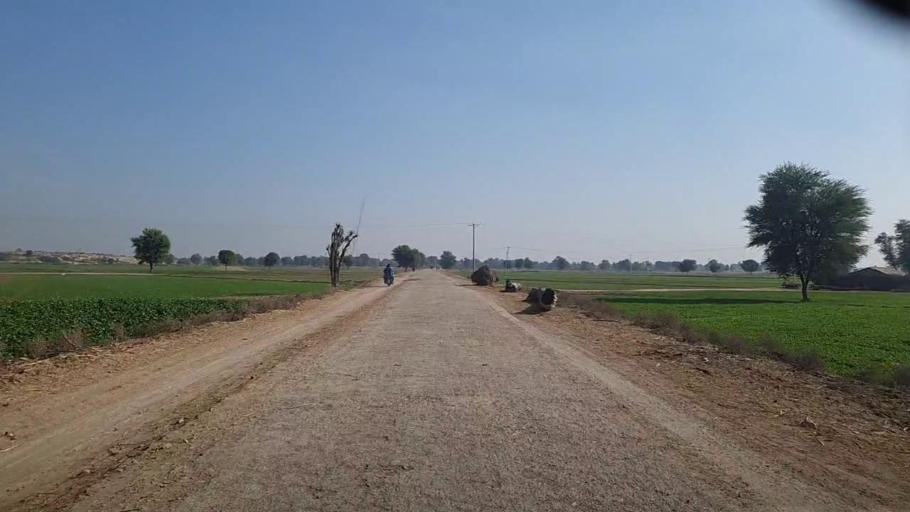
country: PK
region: Sindh
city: Darya Khan Marri
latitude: 26.6678
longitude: 68.3338
